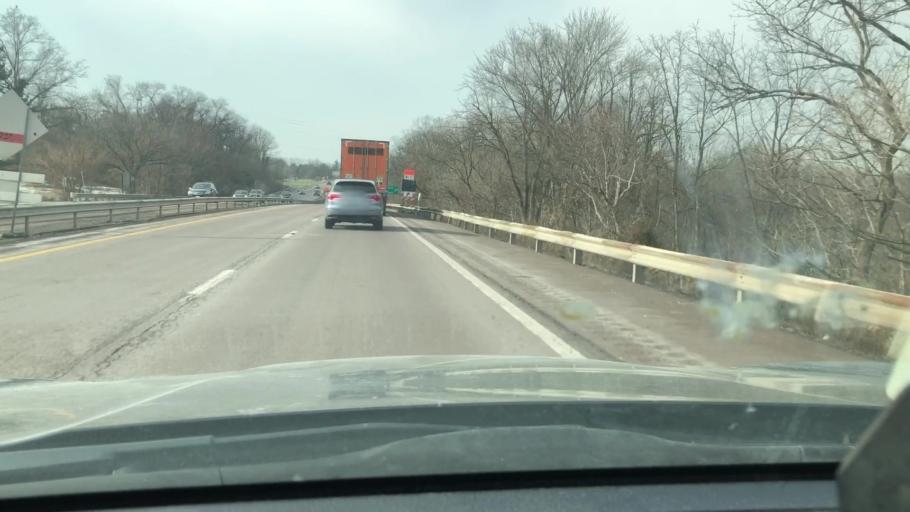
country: US
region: Pennsylvania
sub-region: Chester County
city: South Pottstown
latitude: 40.2382
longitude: -75.6526
